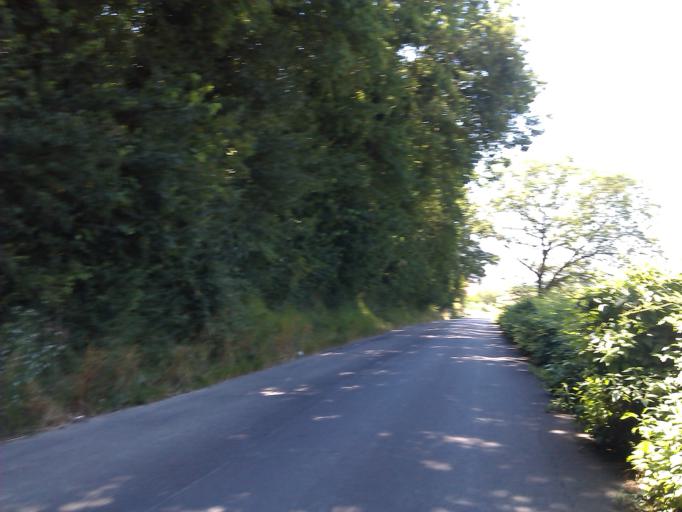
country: IT
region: Umbria
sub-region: Provincia di Terni
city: Fabro Scalo
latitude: 42.8578
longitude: 12.0438
